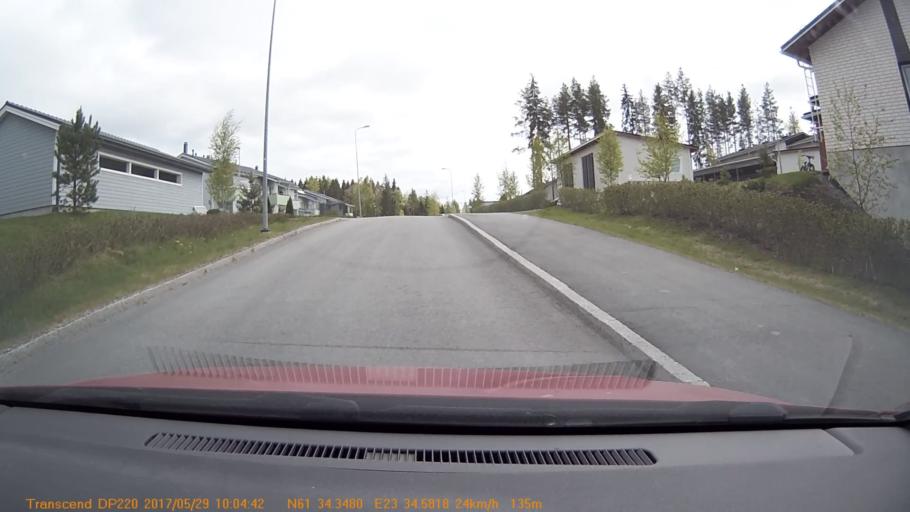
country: FI
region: Pirkanmaa
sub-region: Tampere
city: Yloejaervi
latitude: 61.5725
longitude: 23.5764
